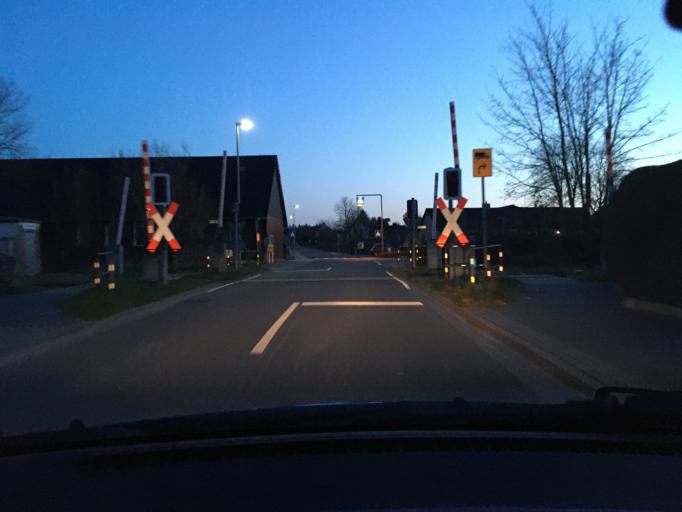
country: DE
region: Lower Saxony
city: Barum
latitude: 52.9965
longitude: 10.5089
